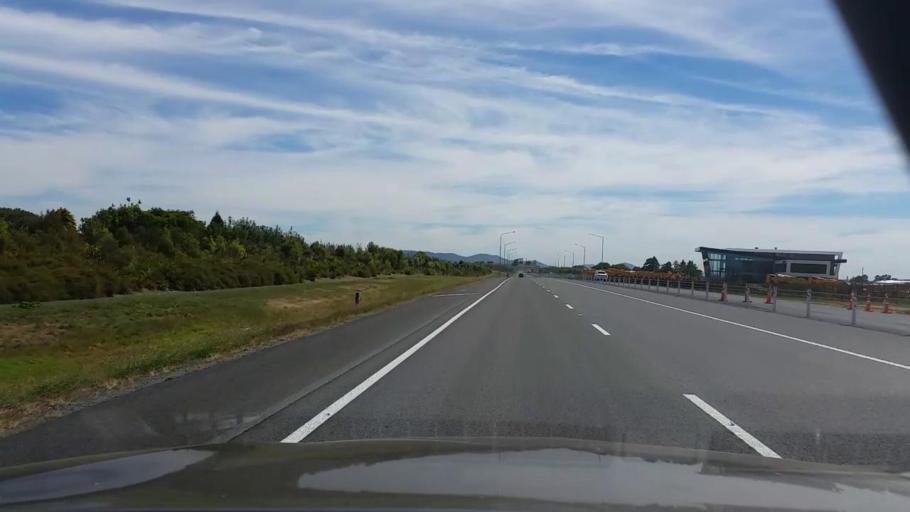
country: NZ
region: Waikato
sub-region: Hamilton City
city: Hamilton
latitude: -37.7424
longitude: 175.2135
